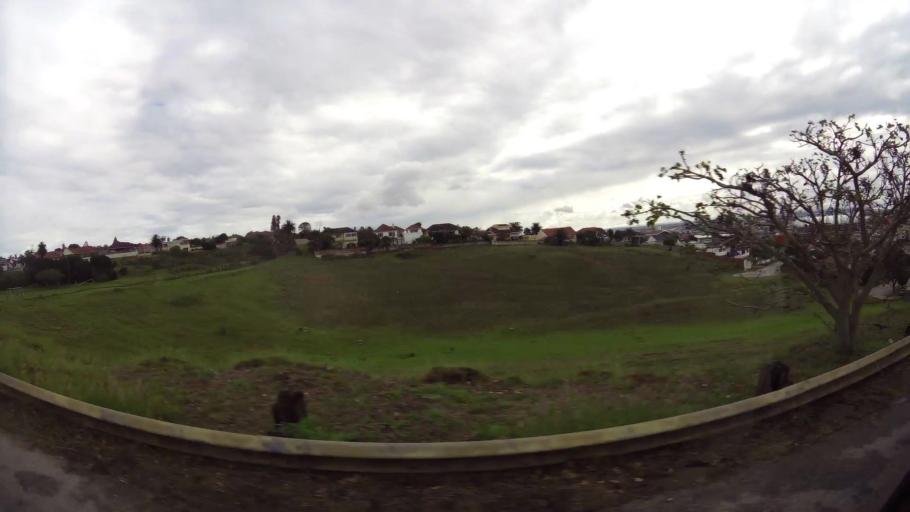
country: ZA
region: Eastern Cape
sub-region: Nelson Mandela Bay Metropolitan Municipality
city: Port Elizabeth
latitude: -33.9483
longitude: 25.5962
